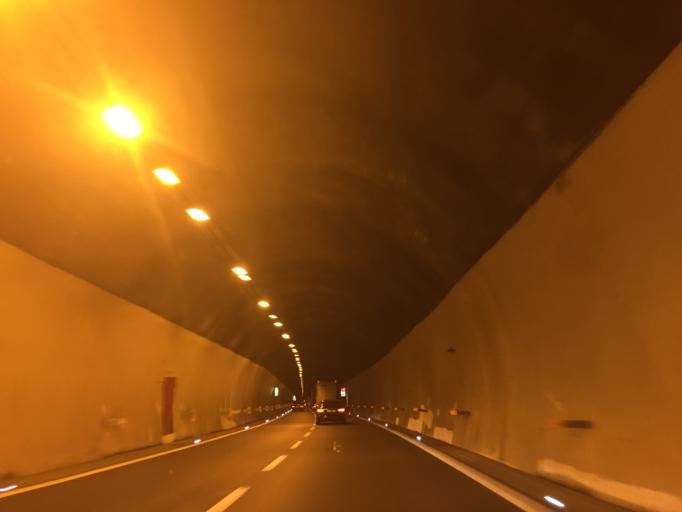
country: IT
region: Tuscany
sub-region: Provincia di Lucca
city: Massarosa
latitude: 43.8529
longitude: 10.3753
